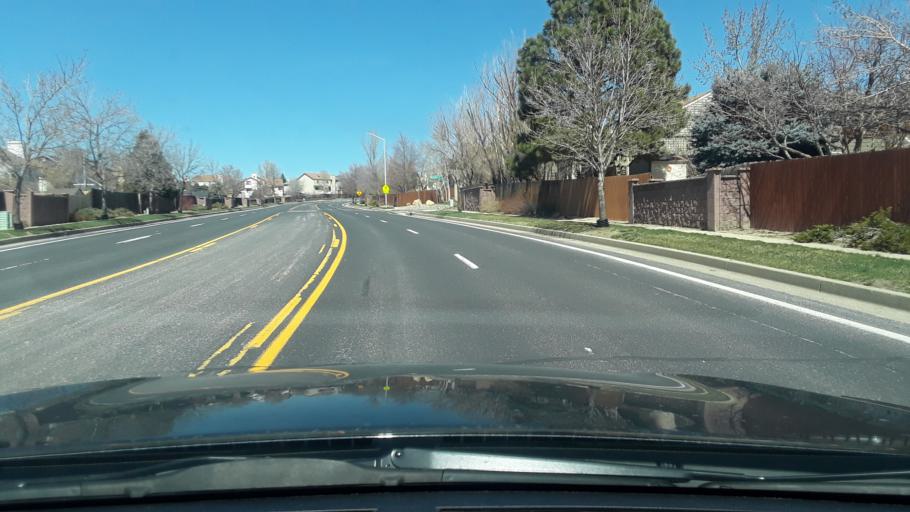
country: US
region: Colorado
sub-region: El Paso County
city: Black Forest
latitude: 38.9583
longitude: -104.7500
